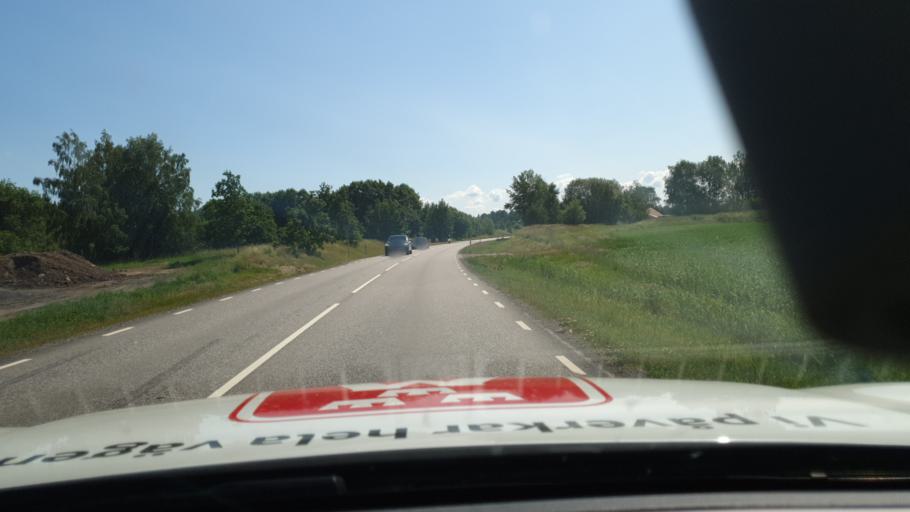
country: SE
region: Vaestra Goetaland
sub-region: Lidkopings Kommun
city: Lidkoping
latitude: 58.5413
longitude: 13.1134
